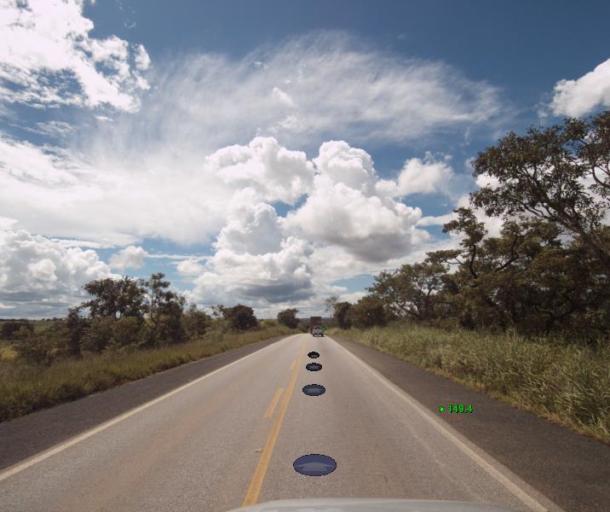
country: BR
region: Goias
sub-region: Uruacu
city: Uruacu
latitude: -14.0807
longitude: -49.0983
